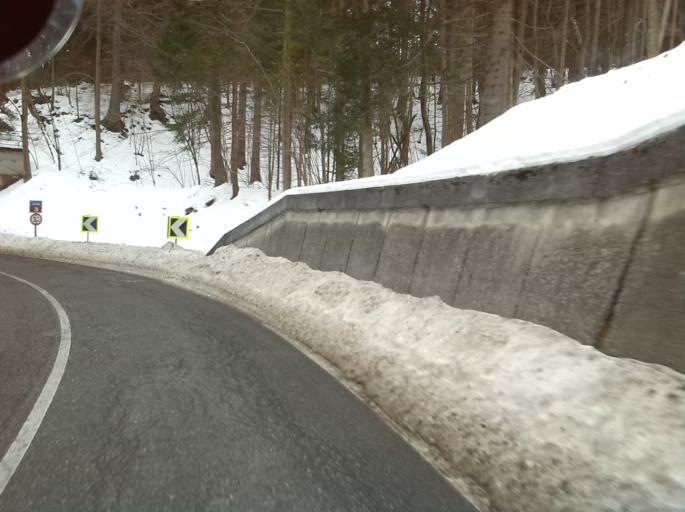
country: IT
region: Friuli Venezia Giulia
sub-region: Provincia di Udine
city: Tarvisio
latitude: 46.5050
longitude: 13.6199
